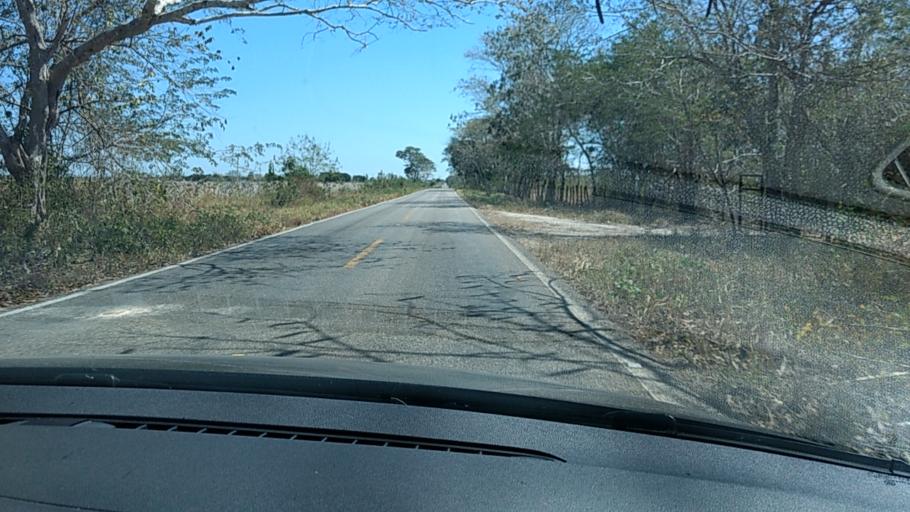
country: MX
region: Yucatan
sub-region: Tizimin
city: Tizimin
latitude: 21.2068
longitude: -88.2031
